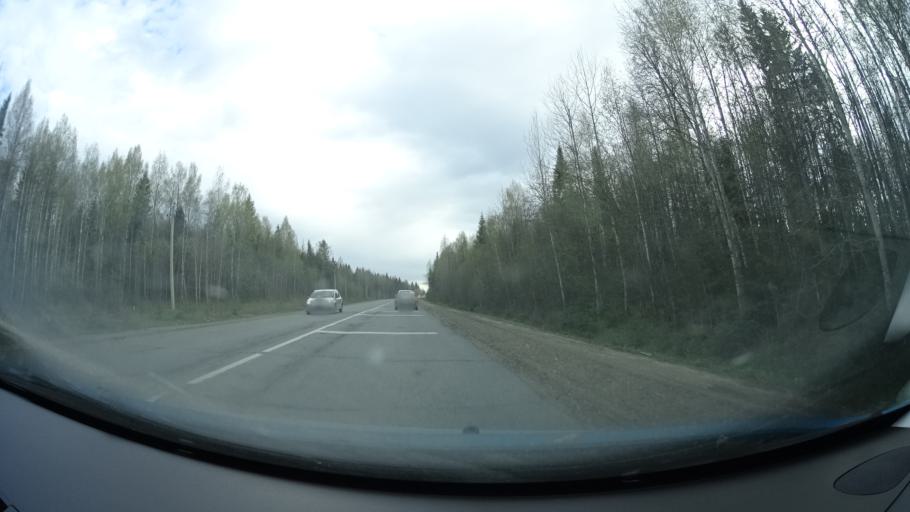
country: RU
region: Perm
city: Kultayevo
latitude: 57.7914
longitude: 55.7757
